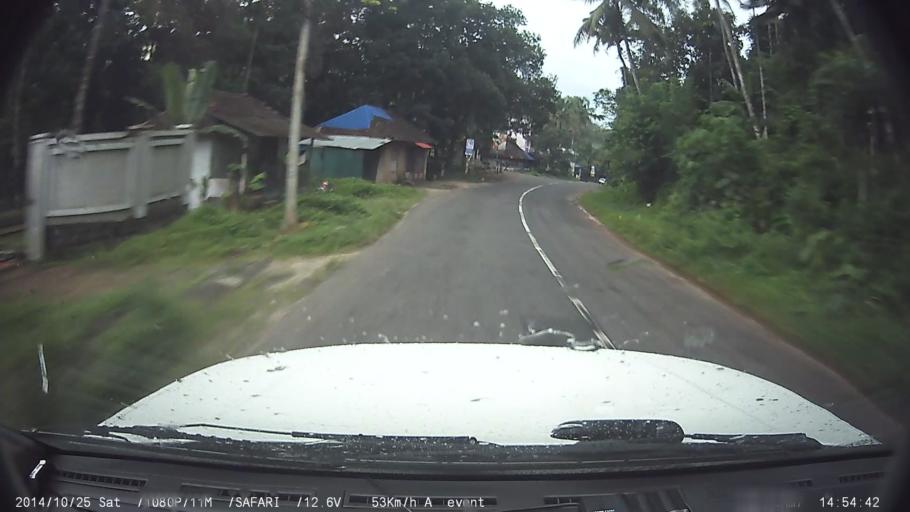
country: IN
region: Kerala
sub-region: Ernakulam
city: Piravam
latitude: 9.8823
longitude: 76.5941
